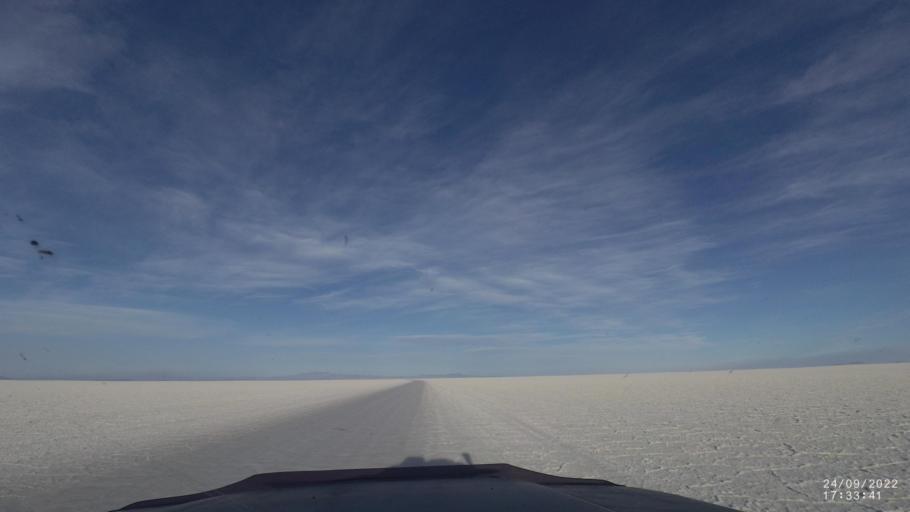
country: BO
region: Potosi
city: Colchani
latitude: -20.3200
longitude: -67.2998
